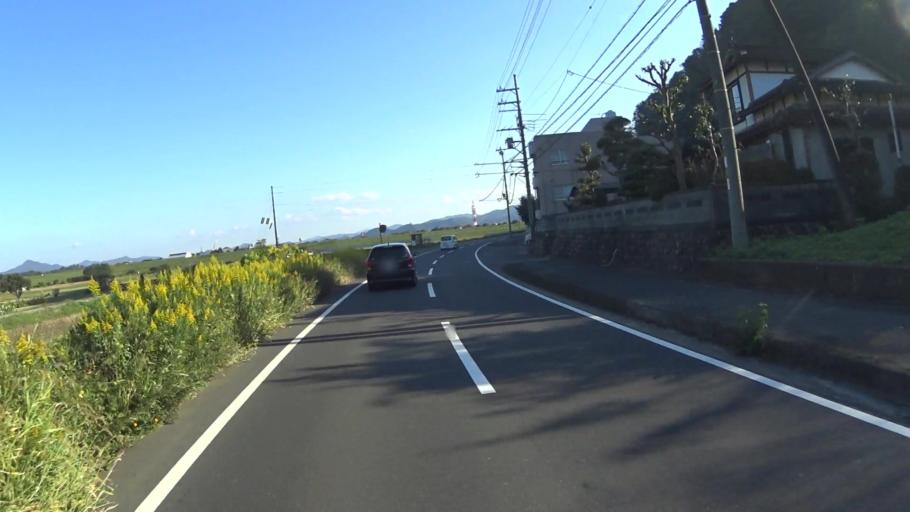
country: JP
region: Kyoto
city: Fukuchiyama
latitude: 35.3186
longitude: 135.1089
